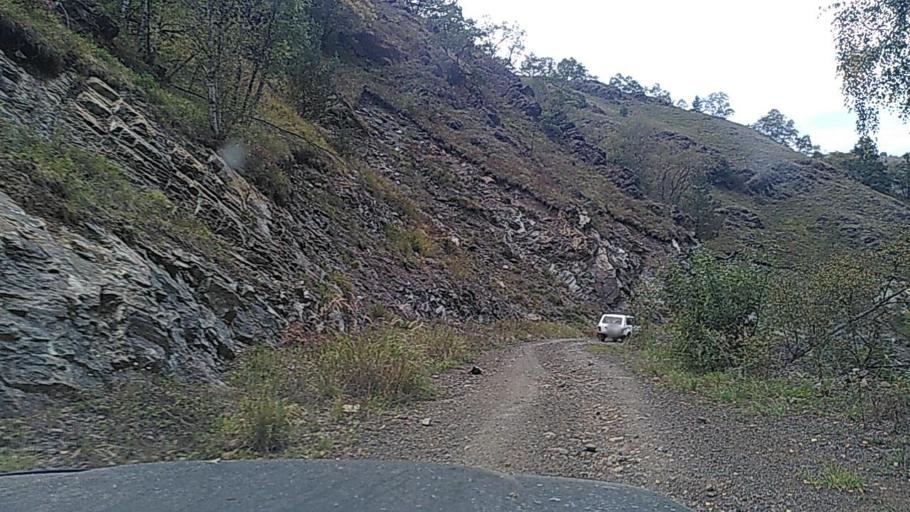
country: RU
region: Kabardino-Balkariya
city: Kamennomostskoye
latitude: 43.7123
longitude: 42.8461
